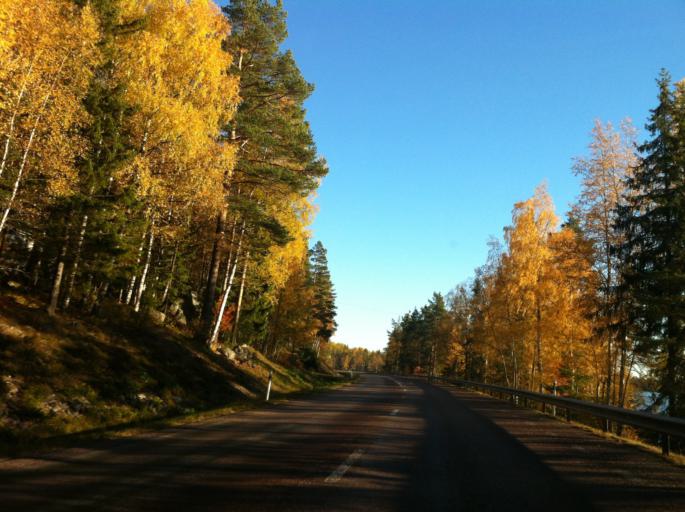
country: SE
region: Dalarna
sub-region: Faluns Kommun
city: Bjursas
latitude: 60.7628
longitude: 15.3208
